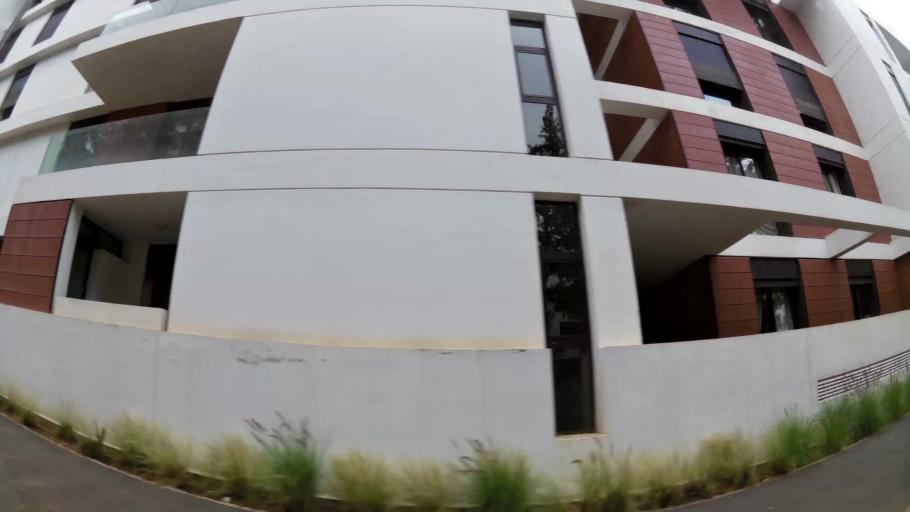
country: MA
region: Rabat-Sale-Zemmour-Zaer
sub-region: Rabat
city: Rabat
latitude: 33.9506
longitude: -6.8331
